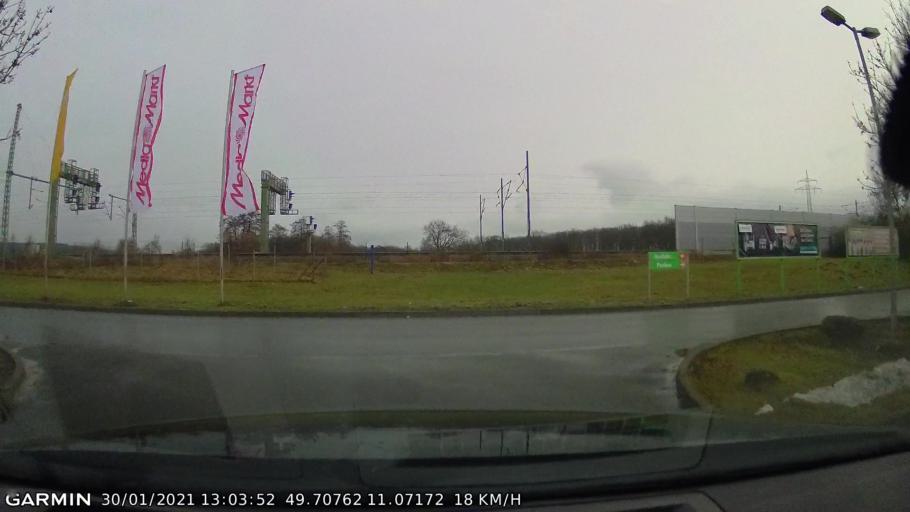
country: DE
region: Bavaria
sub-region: Upper Franconia
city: Forchheim
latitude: 49.7069
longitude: 11.0734
